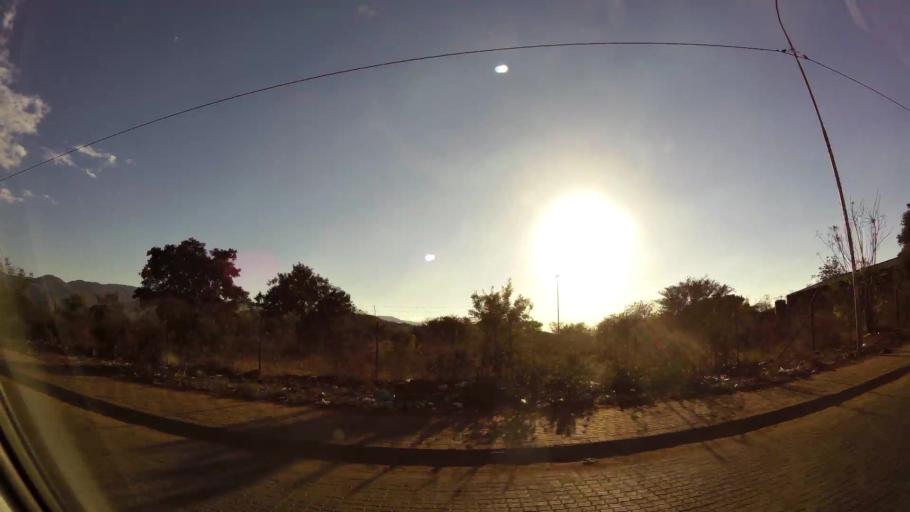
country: ZA
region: Limpopo
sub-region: Waterberg District Municipality
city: Mokopane
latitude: -24.1576
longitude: 28.9885
